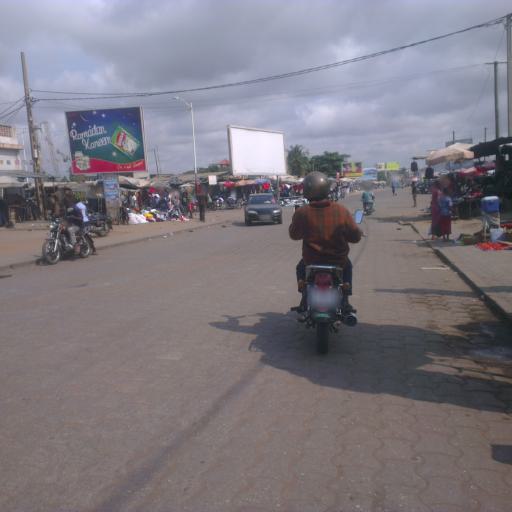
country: TG
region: Maritime
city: Lome
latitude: 6.1538
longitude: 1.2687
